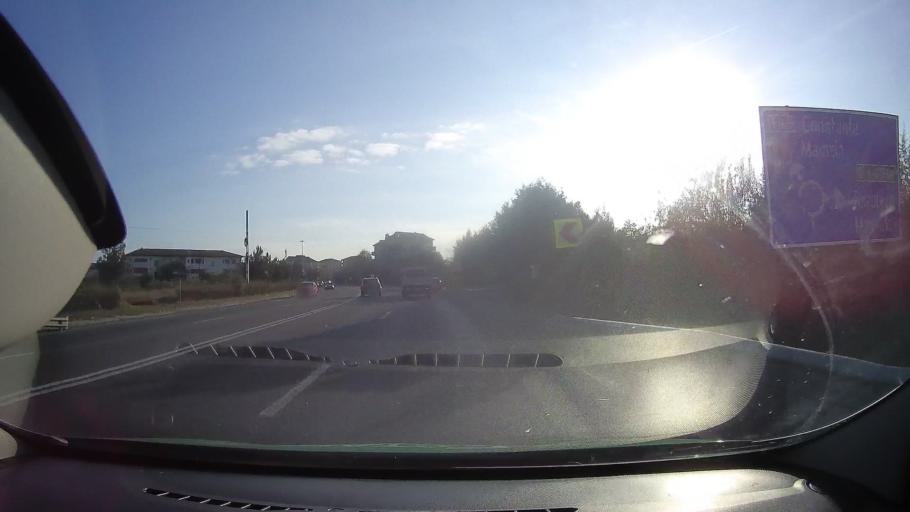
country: RO
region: Constanta
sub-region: Comuna Ovidiu
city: Ovidiu
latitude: 44.2648
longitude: 28.5546
